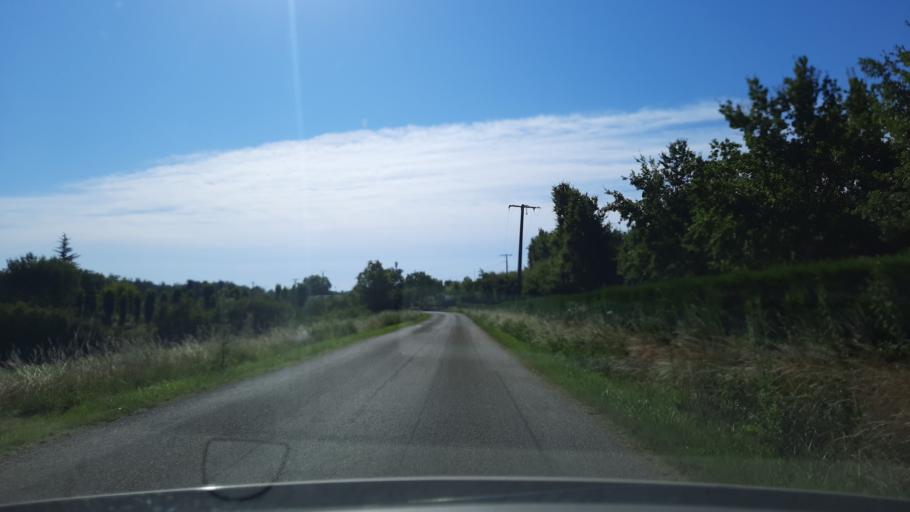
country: FR
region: Midi-Pyrenees
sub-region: Departement du Tarn-et-Garonne
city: Molieres
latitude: 44.1856
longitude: 1.3538
